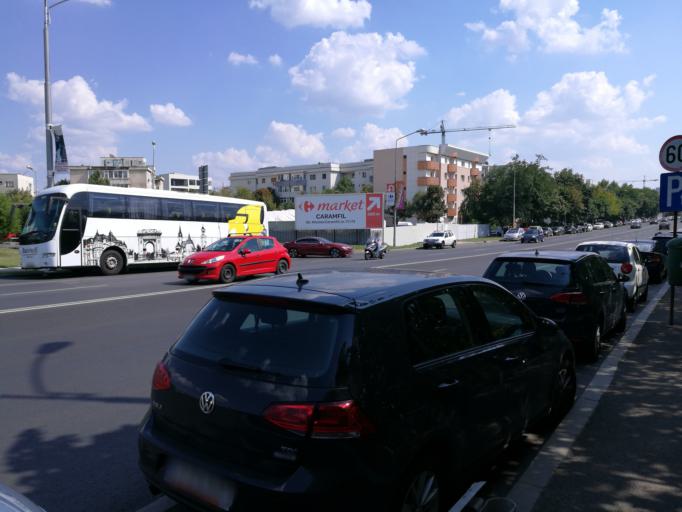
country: RO
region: Bucuresti
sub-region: Municipiul Bucuresti
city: Bucharest
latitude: 44.4868
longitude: 26.0918
